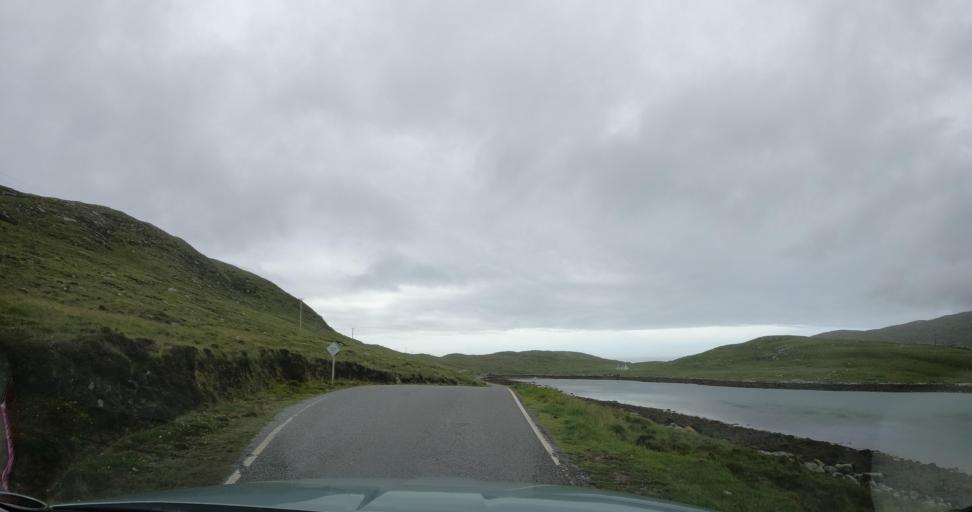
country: GB
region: Scotland
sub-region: Eilean Siar
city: Barra
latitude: 56.9374
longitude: -7.5339
